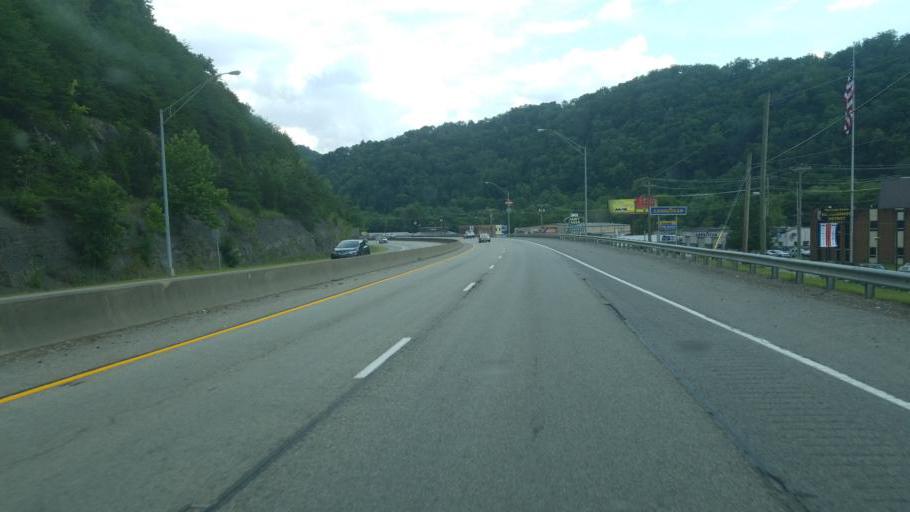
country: US
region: Kentucky
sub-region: Pike County
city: Pikeville
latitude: 37.4699
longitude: -82.5336
